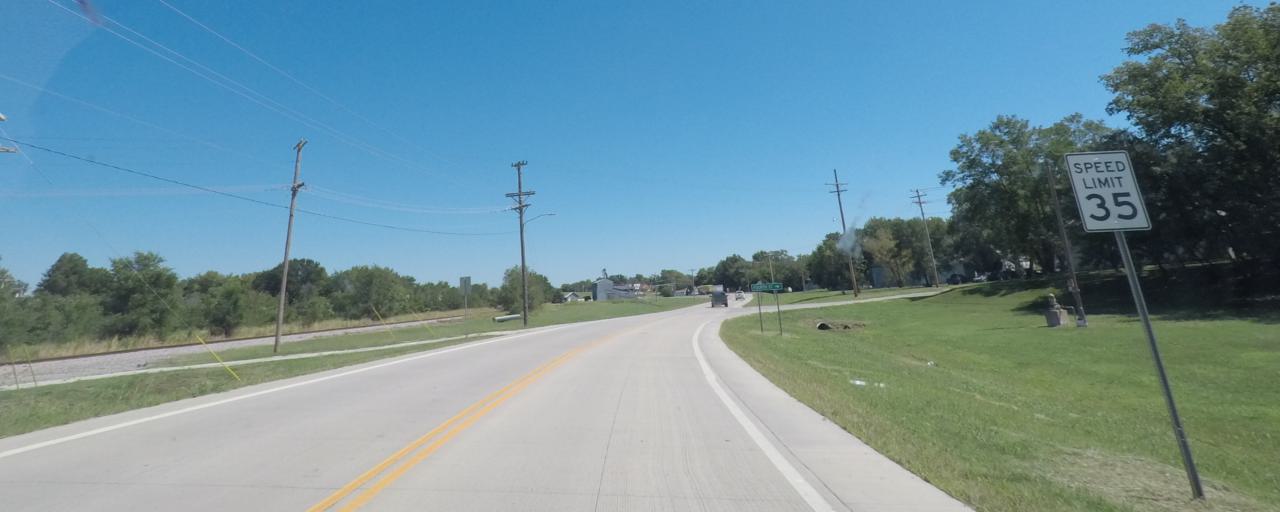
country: US
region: Kansas
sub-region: Sumner County
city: Wellington
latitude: 37.2631
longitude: -97.4066
